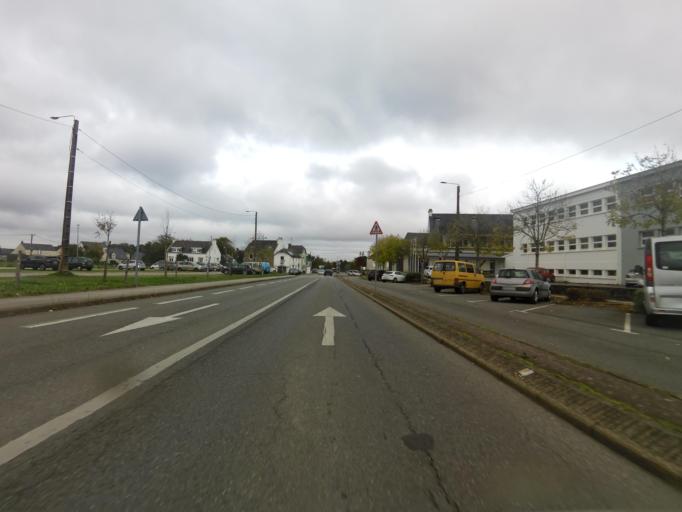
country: FR
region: Brittany
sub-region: Departement du Morbihan
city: Auray
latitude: 47.6707
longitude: -2.9880
